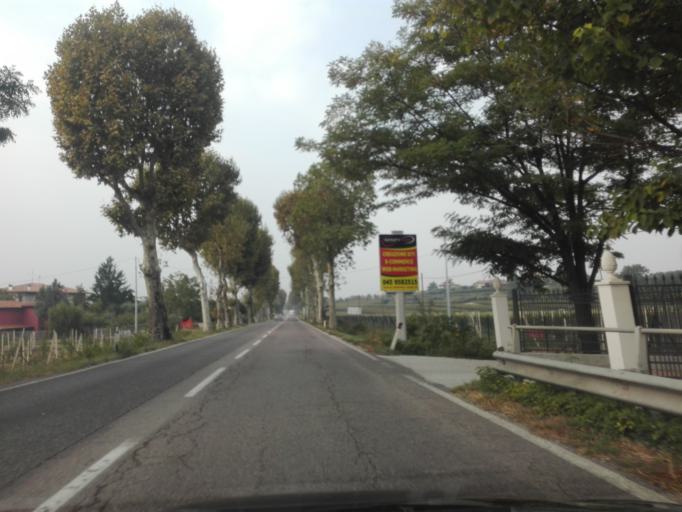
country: IT
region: Veneto
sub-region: Provincia di Verona
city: San Giorgio in Salici
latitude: 45.4417
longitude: 10.8090
